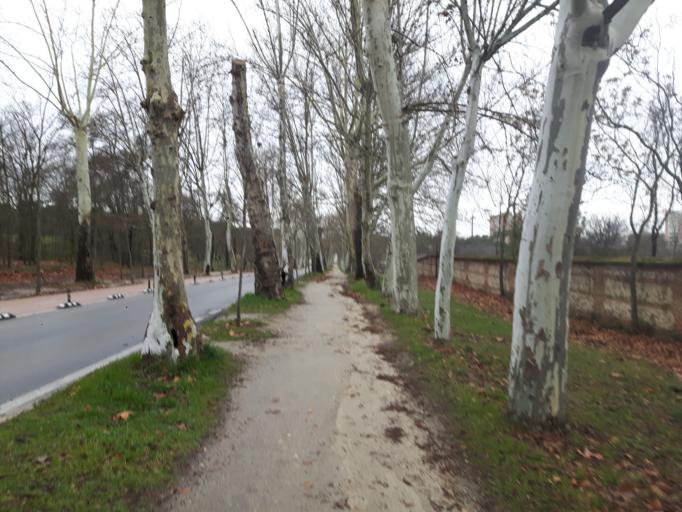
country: ES
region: Madrid
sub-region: Provincia de Madrid
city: Moncloa-Aravaca
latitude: 40.4210
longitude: -3.7299
